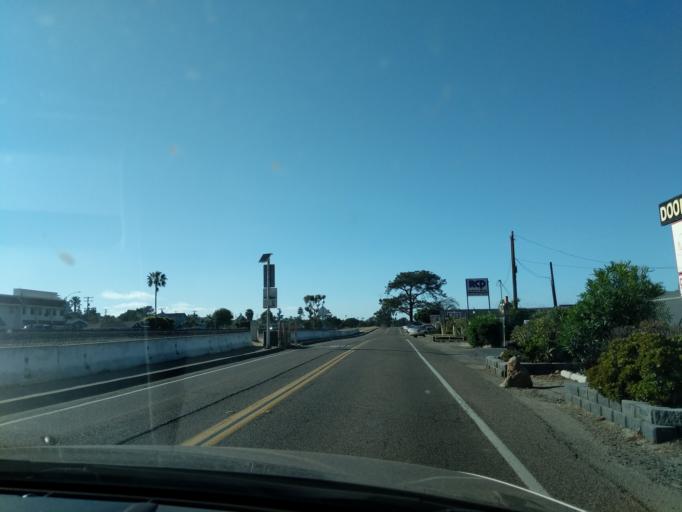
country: US
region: California
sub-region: San Diego County
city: Encinitas
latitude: 33.0588
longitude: -117.2990
